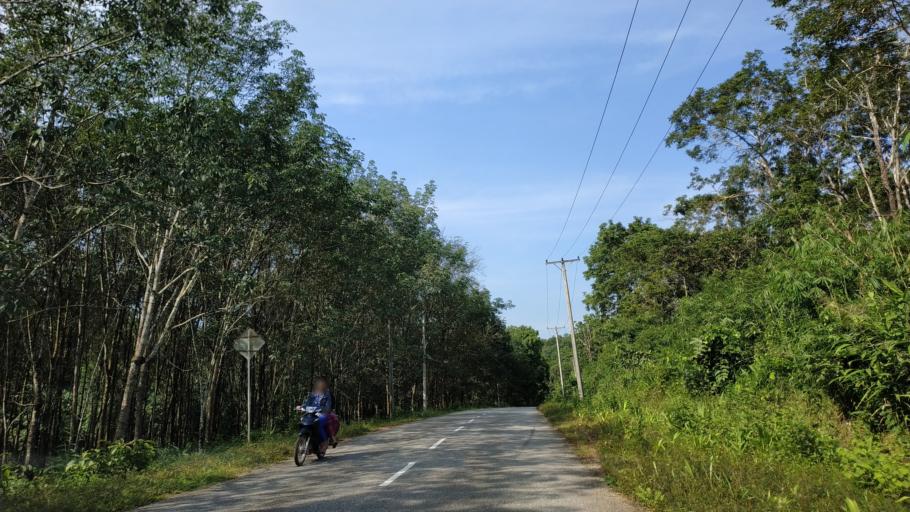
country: TH
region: Kanchanaburi
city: Thong Pha Phum
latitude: 14.6110
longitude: 98.1106
